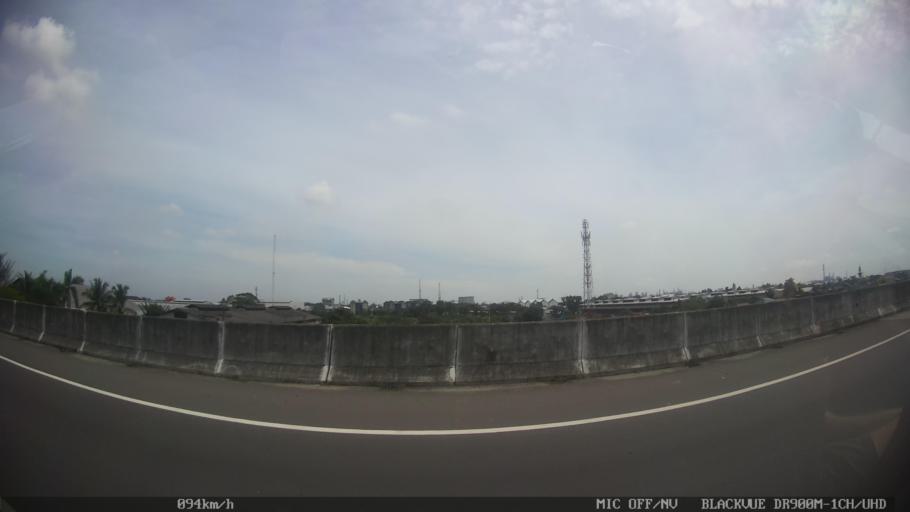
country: ID
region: North Sumatra
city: Medan
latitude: 3.6487
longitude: 98.6640
